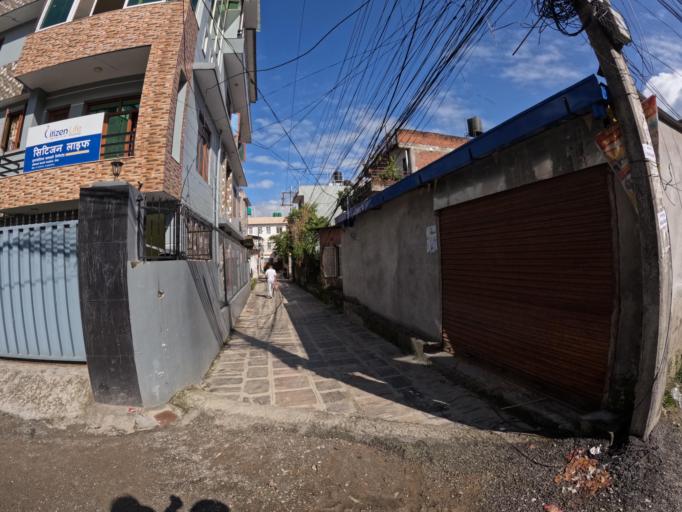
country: NP
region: Central Region
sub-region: Bagmati Zone
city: Kathmandu
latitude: 27.7554
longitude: 85.3298
